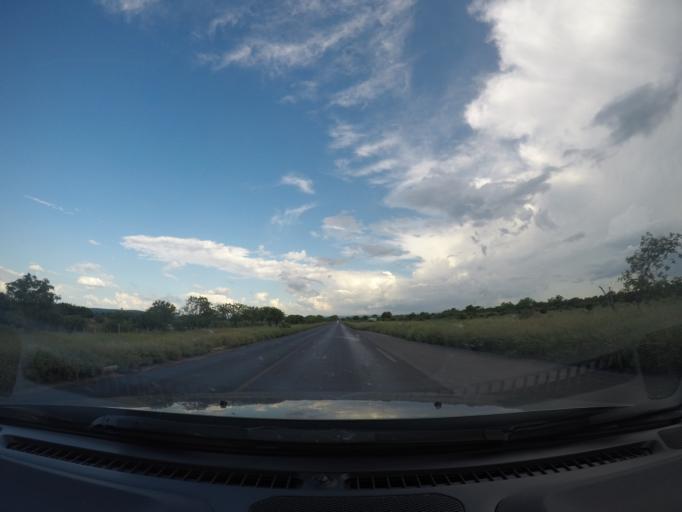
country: BR
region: Bahia
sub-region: Ibotirama
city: Ibotirama
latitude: -12.1374
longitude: -43.3274
